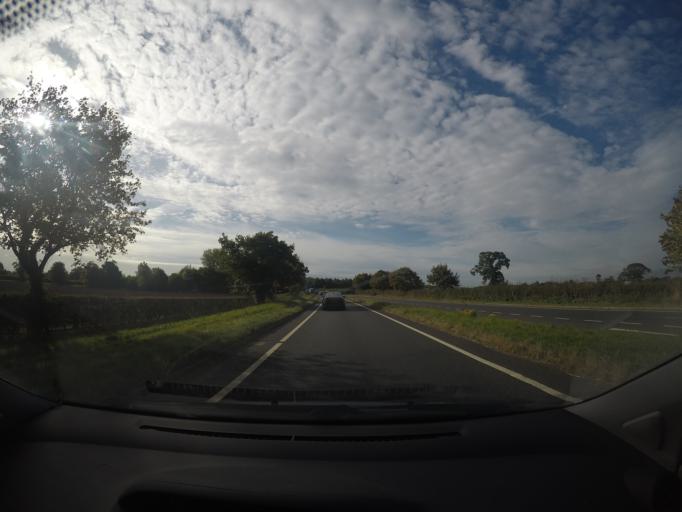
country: GB
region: England
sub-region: City of York
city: Deighton
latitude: 53.8849
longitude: -1.0467
